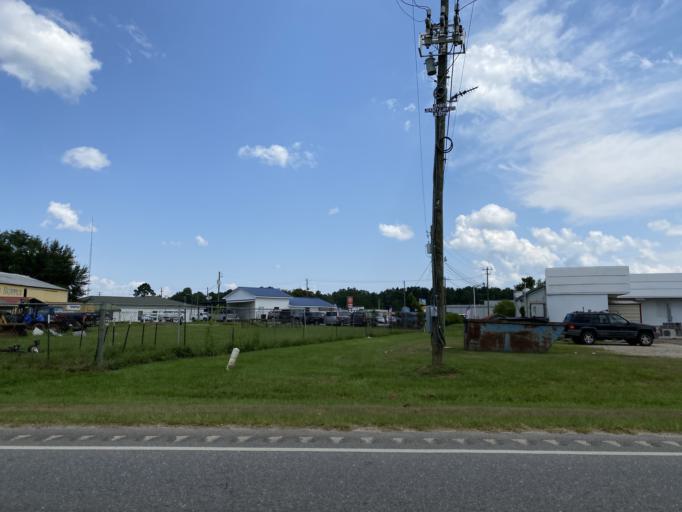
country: US
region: Alabama
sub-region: Wilcox County
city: Camden
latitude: 31.9939
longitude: -87.2791
